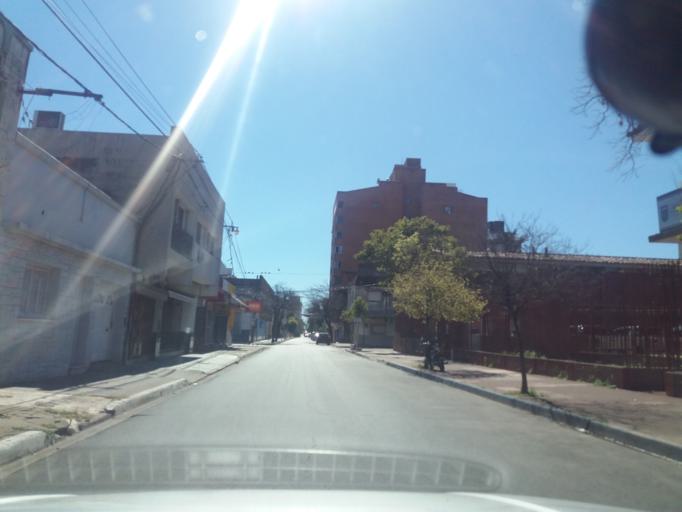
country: AR
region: Corrientes
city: Corrientes
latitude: -27.4738
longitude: -58.8362
